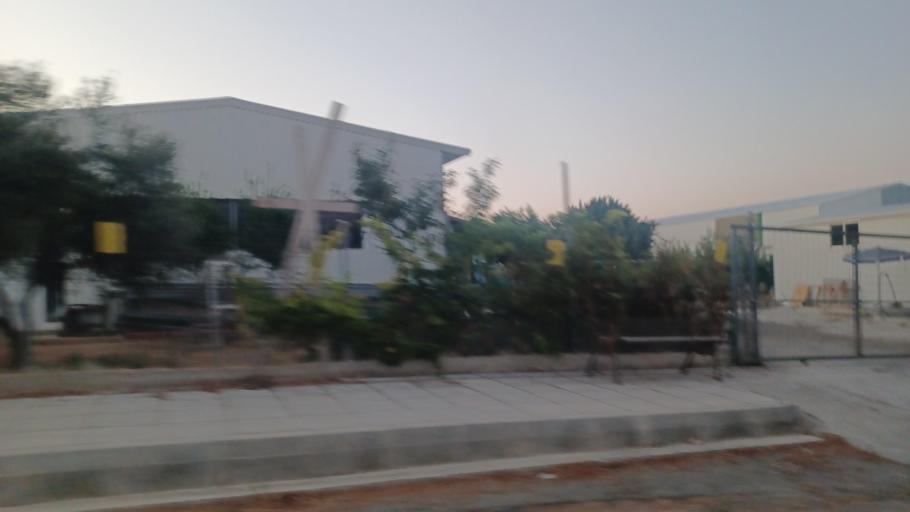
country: CY
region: Pafos
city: Mesogi
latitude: 34.8113
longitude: 32.4425
